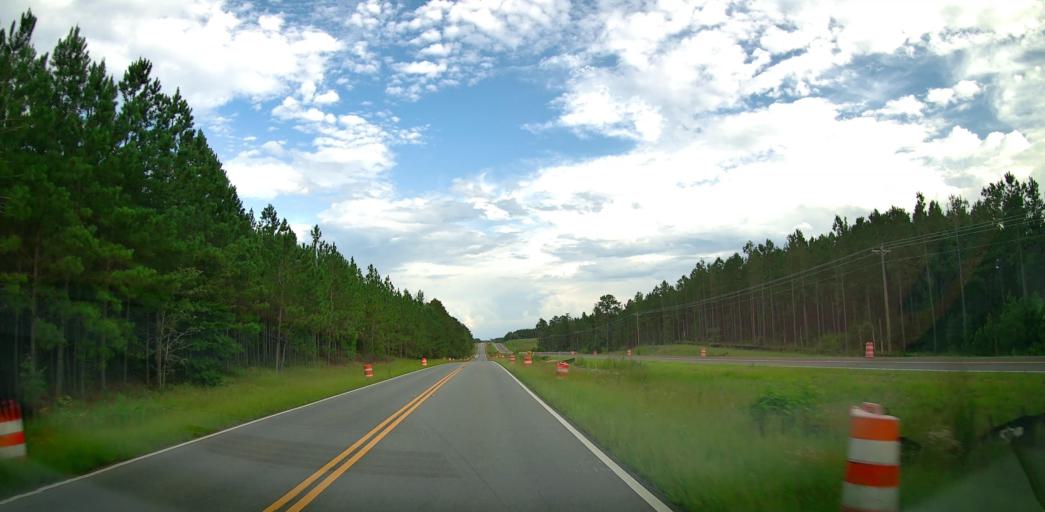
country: US
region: Georgia
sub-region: Bleckley County
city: Cochran
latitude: 32.3272
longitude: -83.2901
